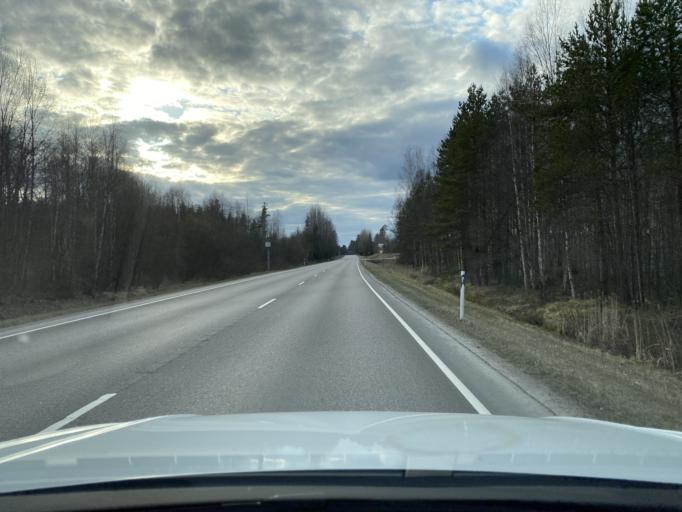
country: FI
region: Haeme
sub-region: Haemeenlinna
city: Renko
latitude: 60.7875
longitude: 24.1339
